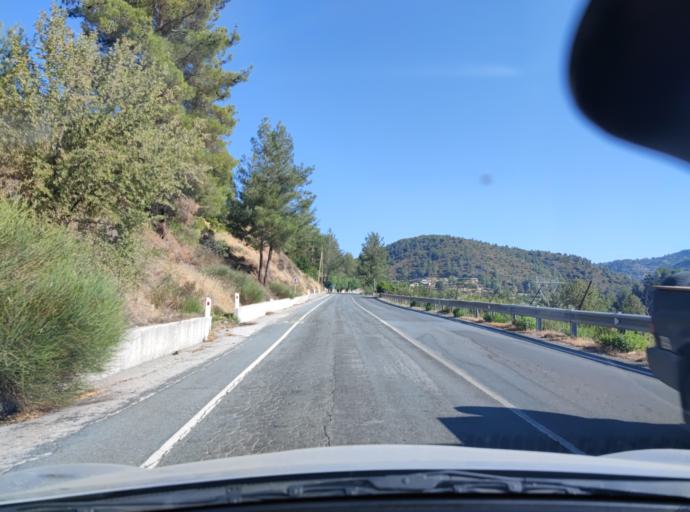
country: CY
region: Limassol
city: Pelendri
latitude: 34.9100
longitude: 32.9428
